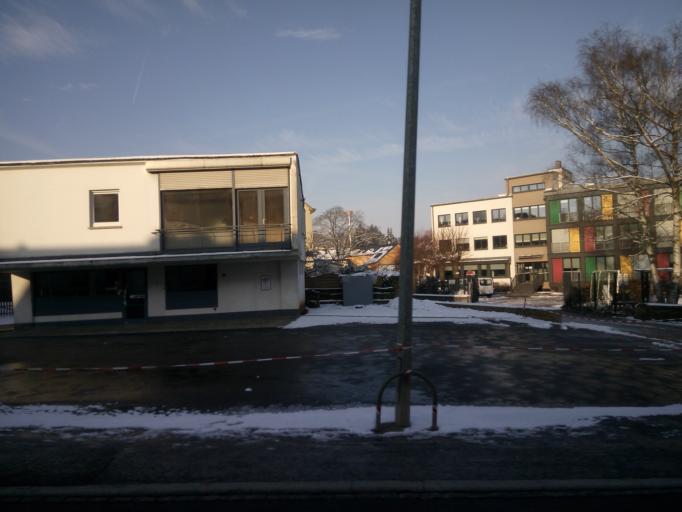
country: LU
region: Grevenmacher
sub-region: Canton de Grevenmacher
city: Junglinster
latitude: 49.7105
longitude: 6.2508
